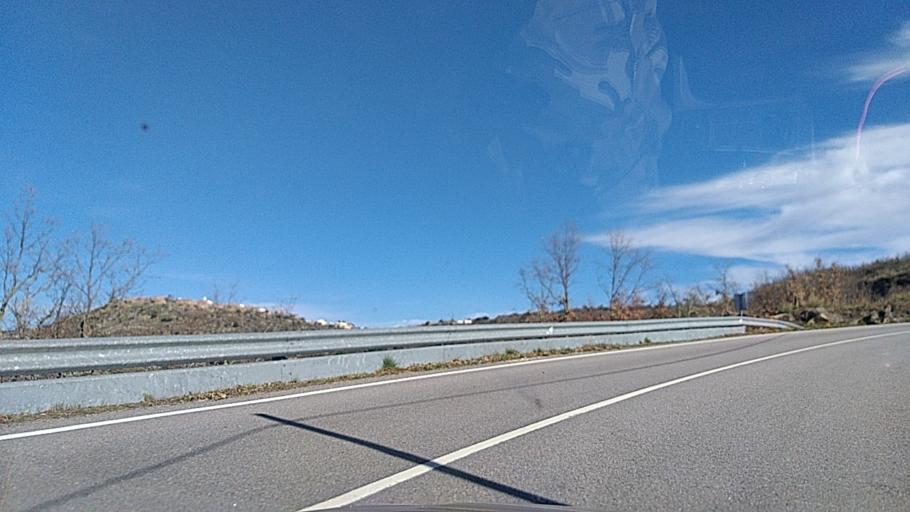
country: ES
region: Castille and Leon
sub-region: Provincia de Salamanca
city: Fuentes de Onoro
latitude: 40.6189
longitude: -6.9128
